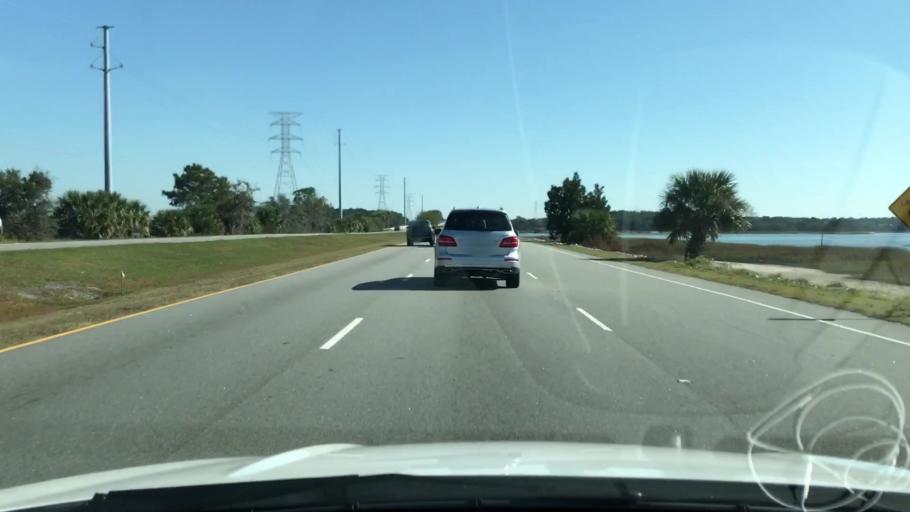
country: US
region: South Carolina
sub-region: Beaufort County
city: Hilton Head Island
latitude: 32.2323
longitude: -80.7968
